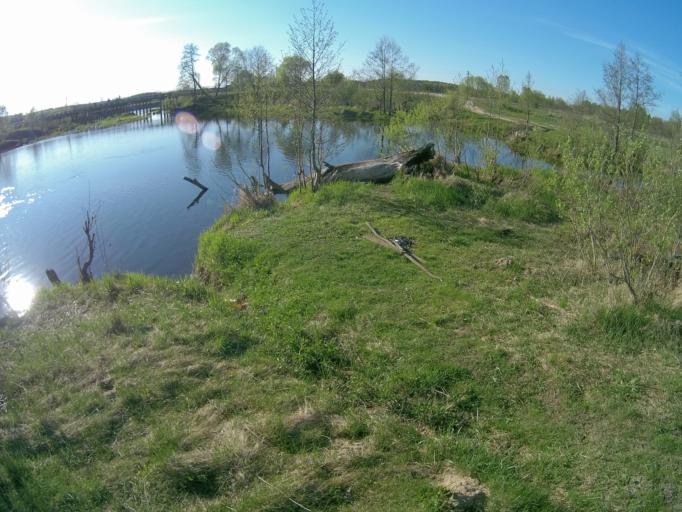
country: RU
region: Vladimir
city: Sudogda
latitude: 56.0626
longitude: 40.8323
